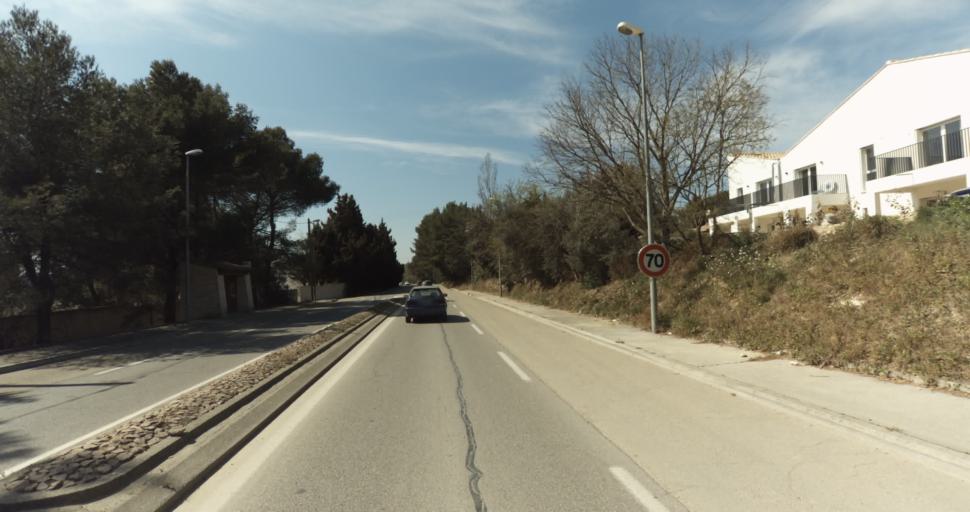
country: FR
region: Provence-Alpes-Cote d'Azur
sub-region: Departement des Bouches-du-Rhone
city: Ventabren
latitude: 43.5463
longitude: 5.2854
